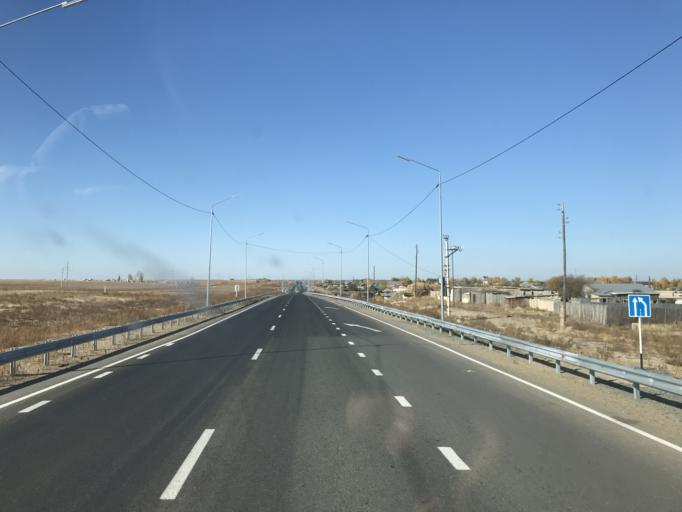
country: RU
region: Altai Krai
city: Malinovoye Ozero
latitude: 50.8809
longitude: 79.4754
